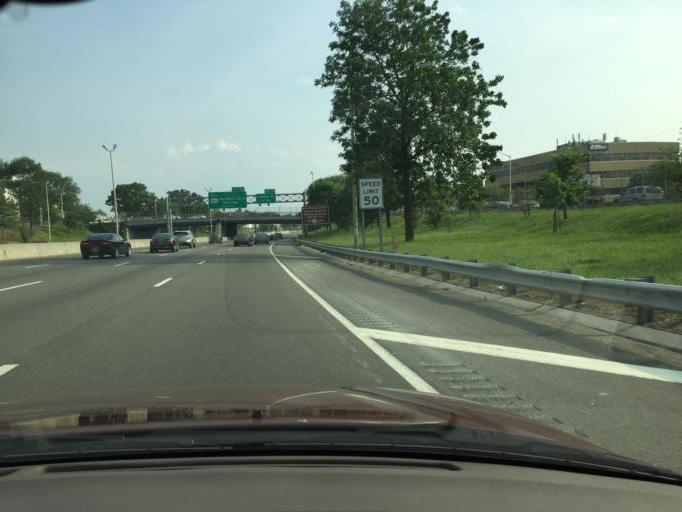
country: US
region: New York
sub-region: Nassau County
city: East Atlantic Beach
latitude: 40.7833
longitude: -73.8249
